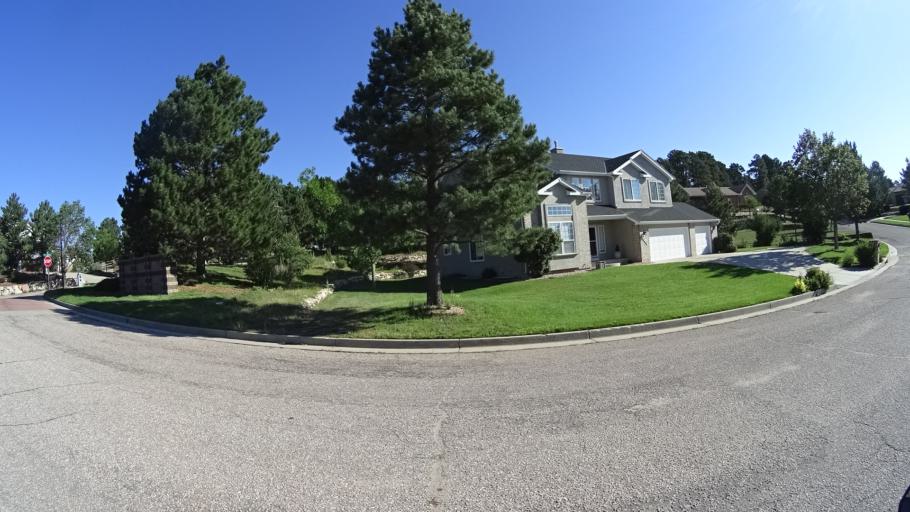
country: US
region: Colorado
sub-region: El Paso County
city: Air Force Academy
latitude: 38.9693
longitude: -104.7927
